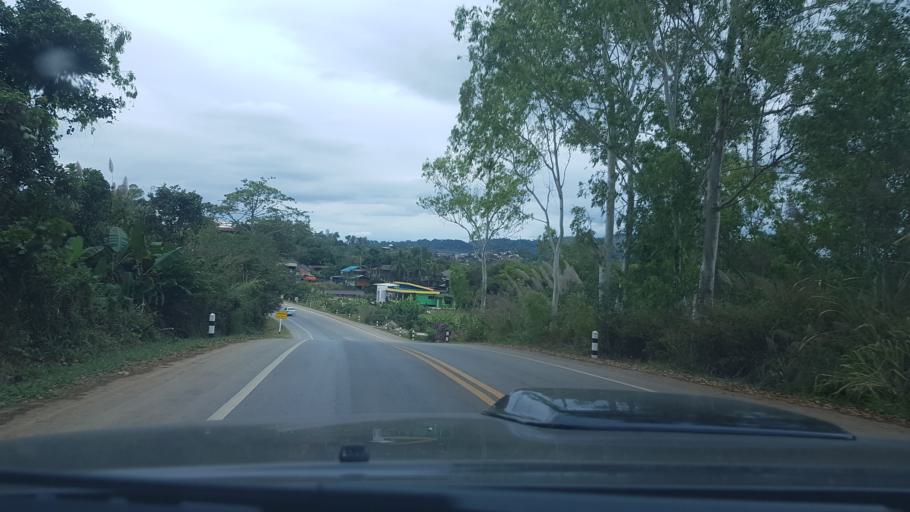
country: TH
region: Phetchabun
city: Khao Kho
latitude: 16.5605
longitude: 101.0176
